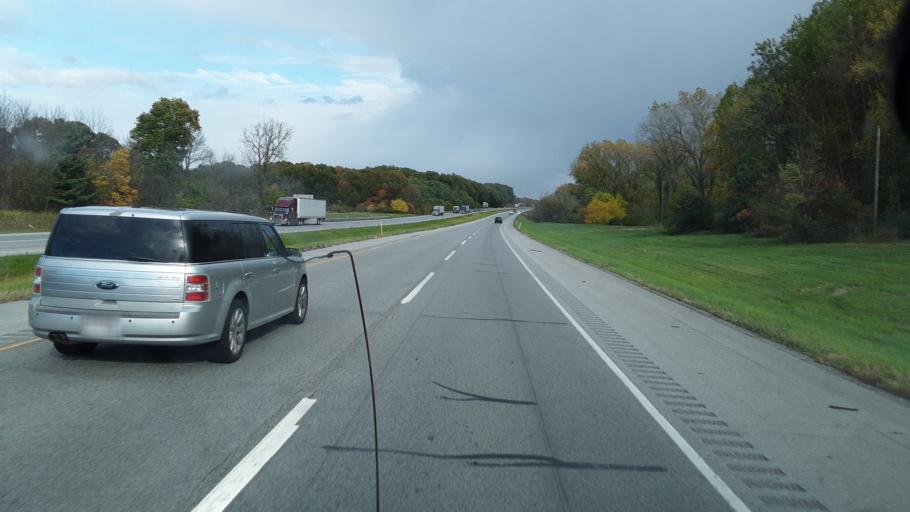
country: US
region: Indiana
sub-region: LaPorte County
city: LaPorte
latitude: 41.6718
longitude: -86.7161
